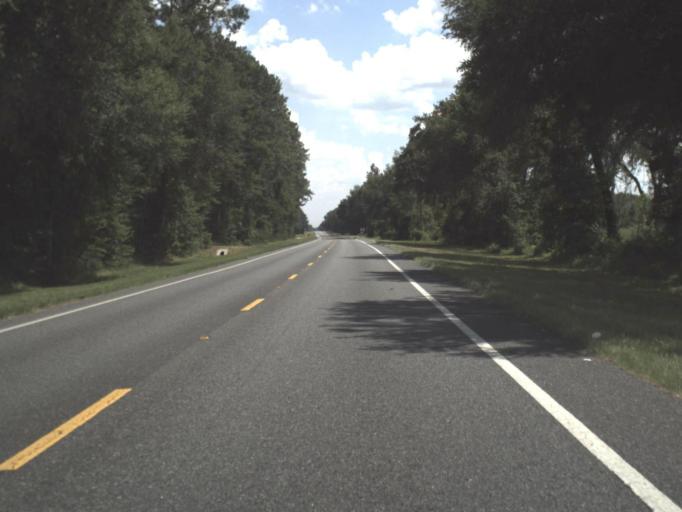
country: US
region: Florida
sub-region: Alachua County
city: High Springs
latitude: 29.9629
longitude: -82.6032
